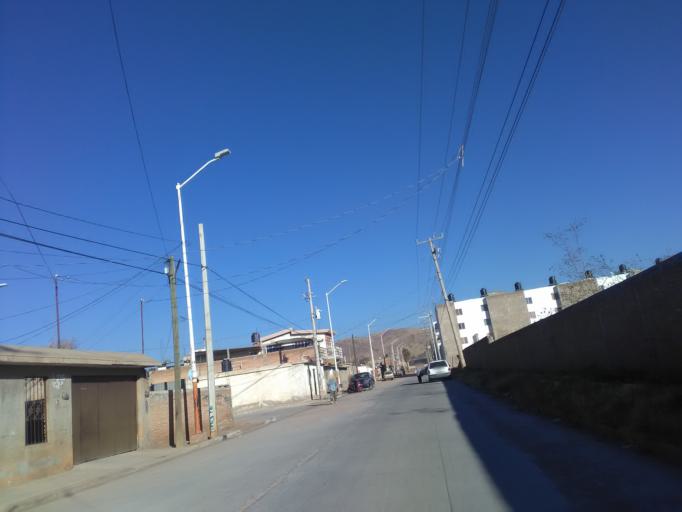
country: MX
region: Durango
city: Victoria de Durango
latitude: 24.0540
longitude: -104.6530
